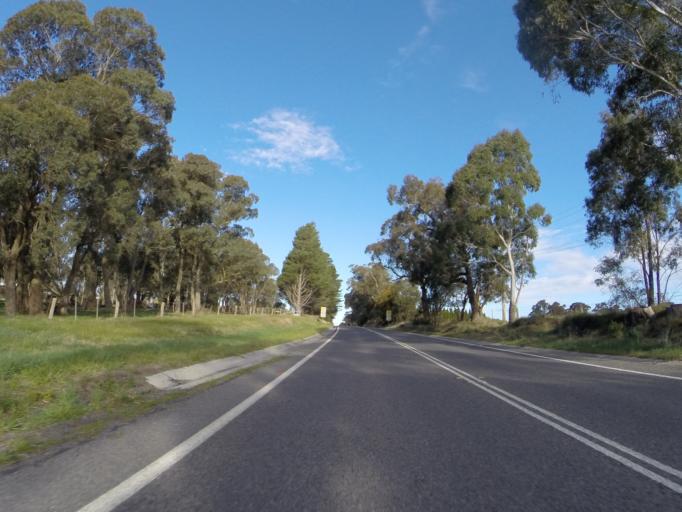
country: AU
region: New South Wales
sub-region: Wingecarribee
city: Moss Vale
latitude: -34.5597
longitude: 150.3968
